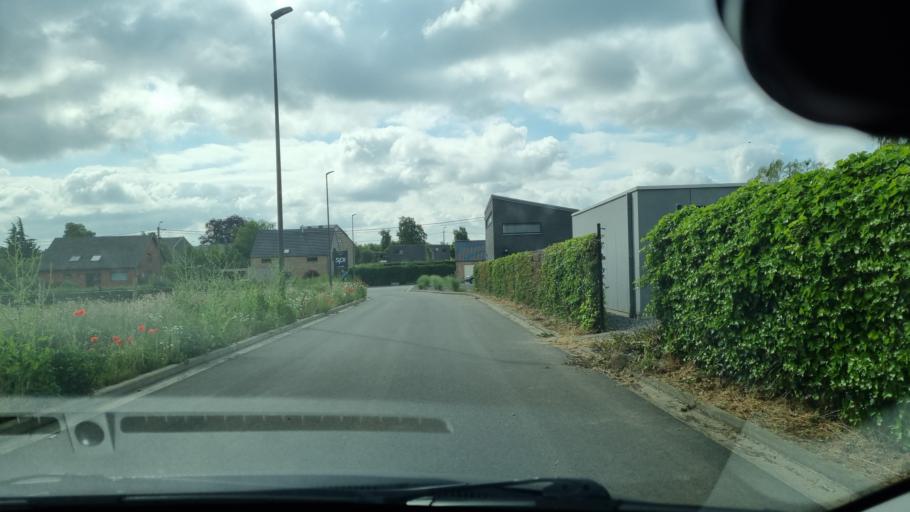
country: BE
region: Wallonia
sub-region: Province de Liege
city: Bassenge
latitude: 50.7371
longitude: 5.6038
